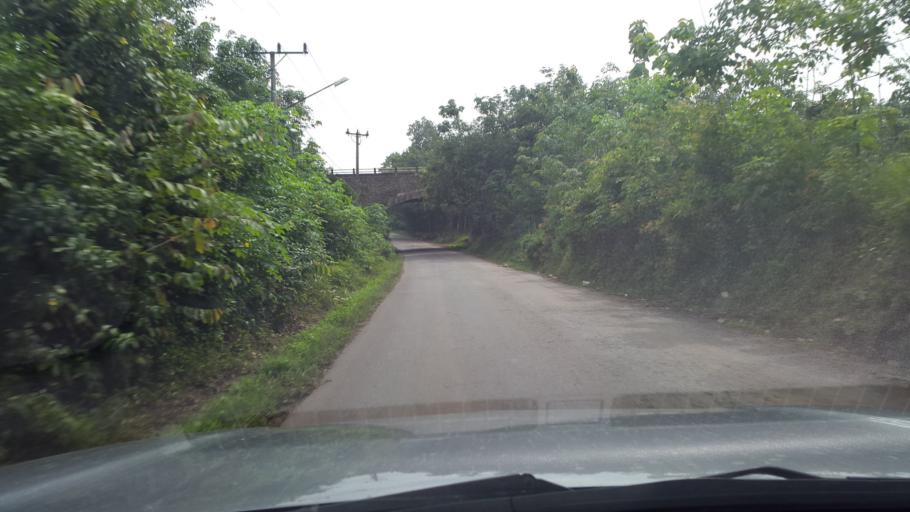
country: ID
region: South Sumatra
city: Gunungmegang Dalam
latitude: -3.3866
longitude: 103.9699
